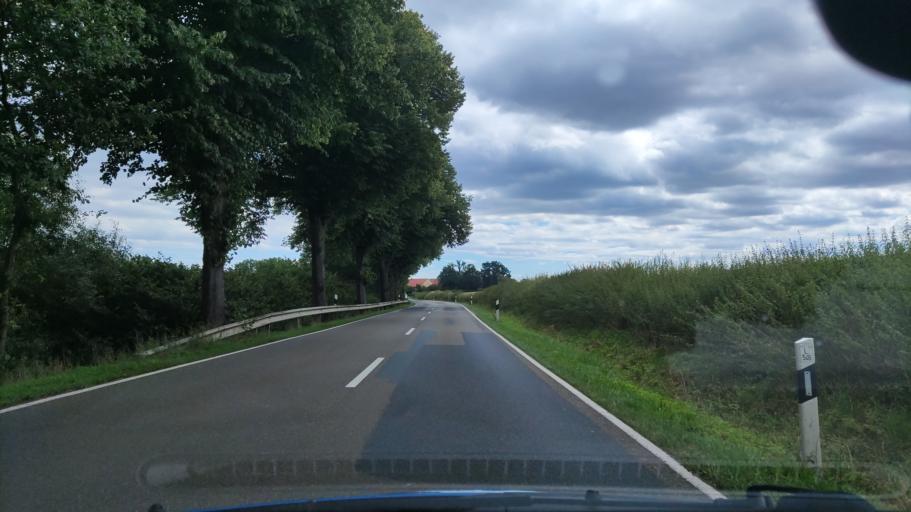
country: DE
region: Lower Saxony
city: Eimen
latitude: 51.8289
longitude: 9.8070
